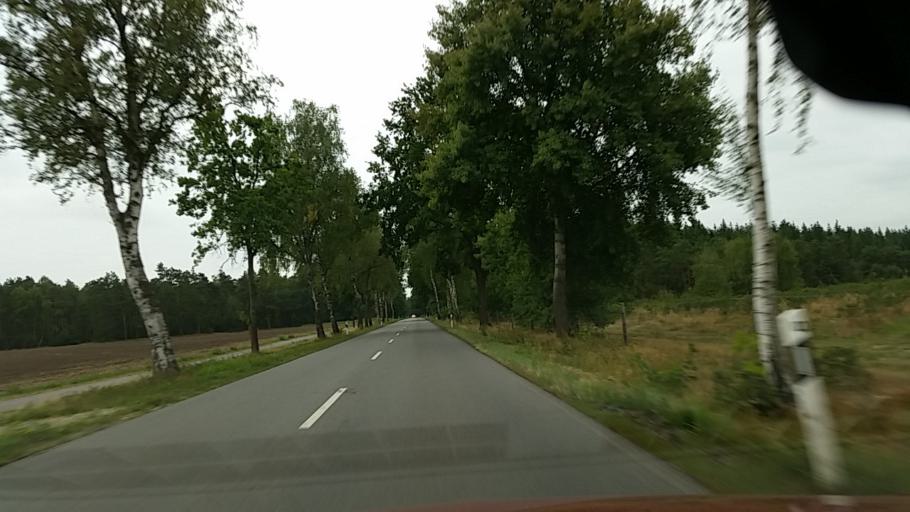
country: DE
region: Lower Saxony
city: Bokensdorf
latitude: 52.5358
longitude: 10.7174
